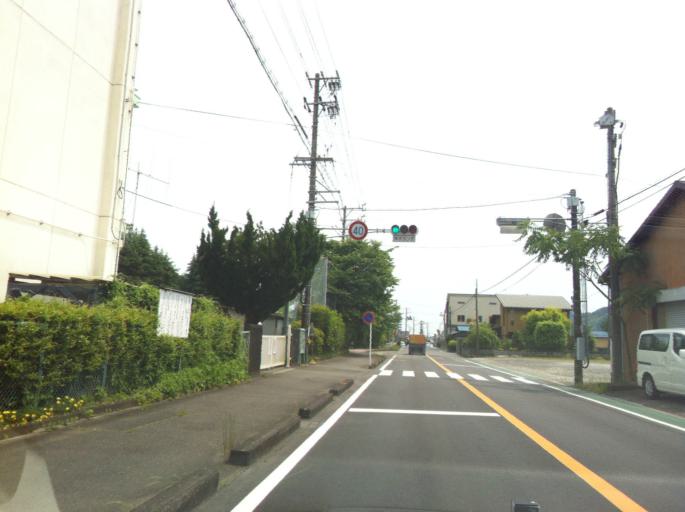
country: JP
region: Shizuoka
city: Shizuoka-shi
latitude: 35.0642
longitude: 138.3700
